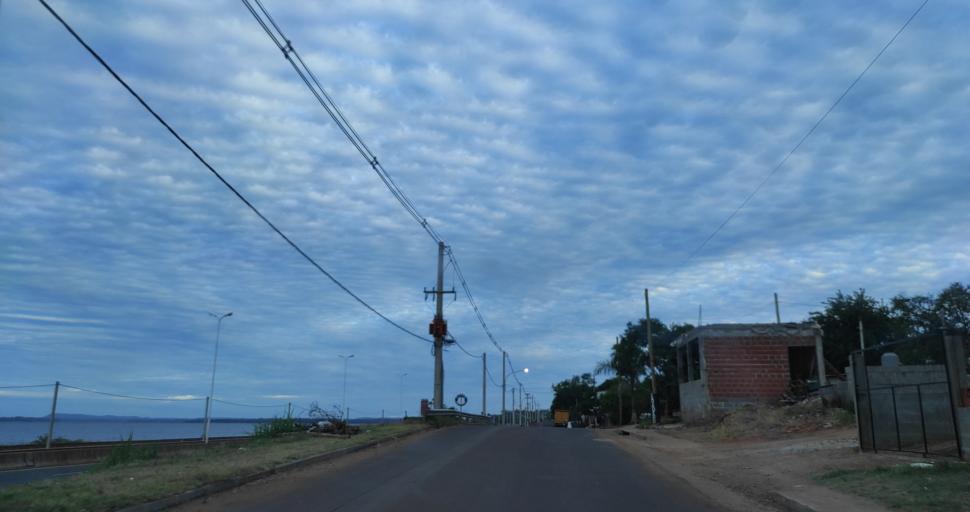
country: AR
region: Misiones
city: Garupa
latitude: -27.4376
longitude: -55.8577
